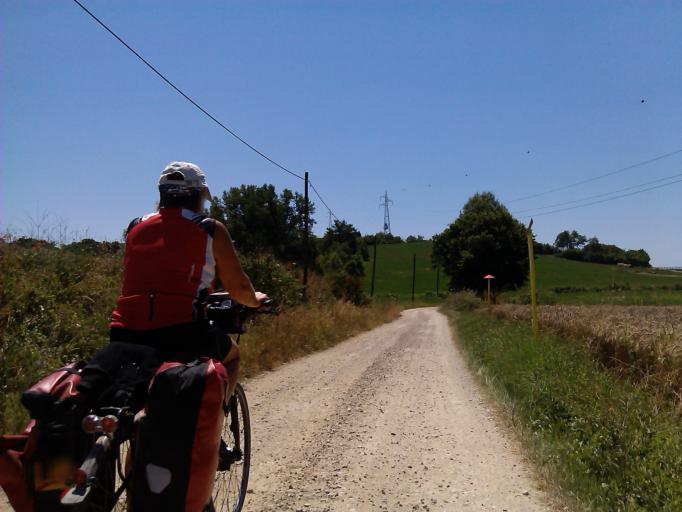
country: IT
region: Umbria
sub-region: Provincia di Terni
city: Ficulle
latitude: 42.8428
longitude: 12.0429
